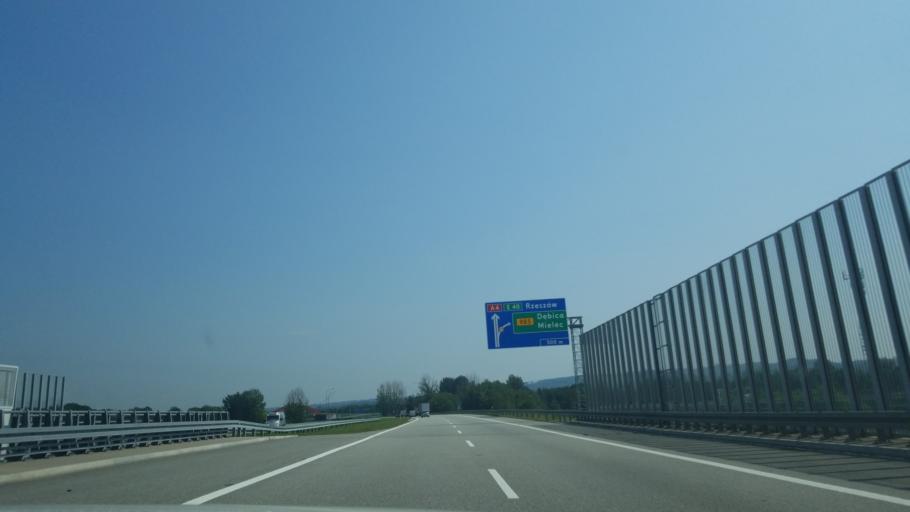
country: PL
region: Subcarpathian Voivodeship
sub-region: Powiat debicki
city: Brzeznica
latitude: 50.0814
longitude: 21.4590
